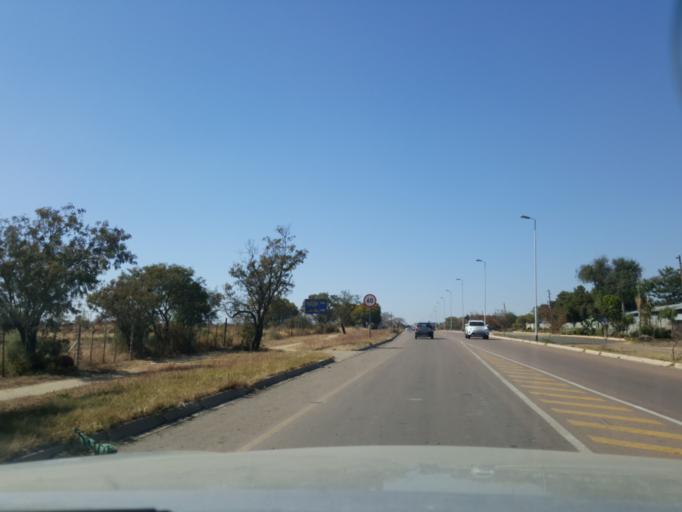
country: ZA
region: Gauteng
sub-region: City of Tshwane Metropolitan Municipality
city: Pretoria
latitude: -25.6539
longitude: 28.1976
